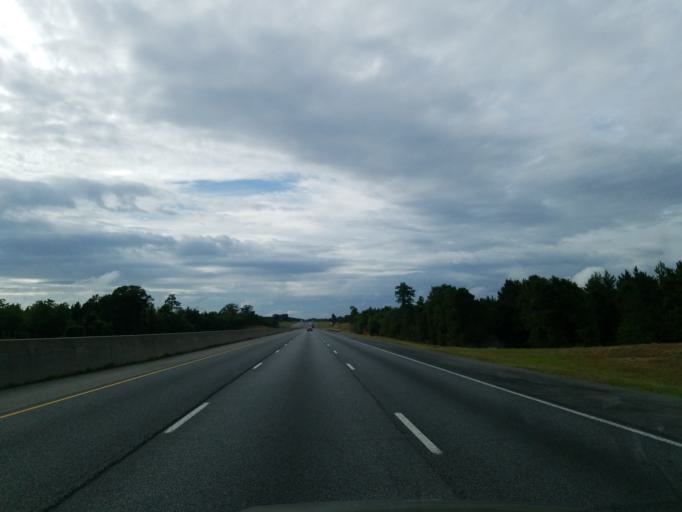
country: US
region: Georgia
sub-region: Turner County
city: Ashburn
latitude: 31.7952
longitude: -83.6970
